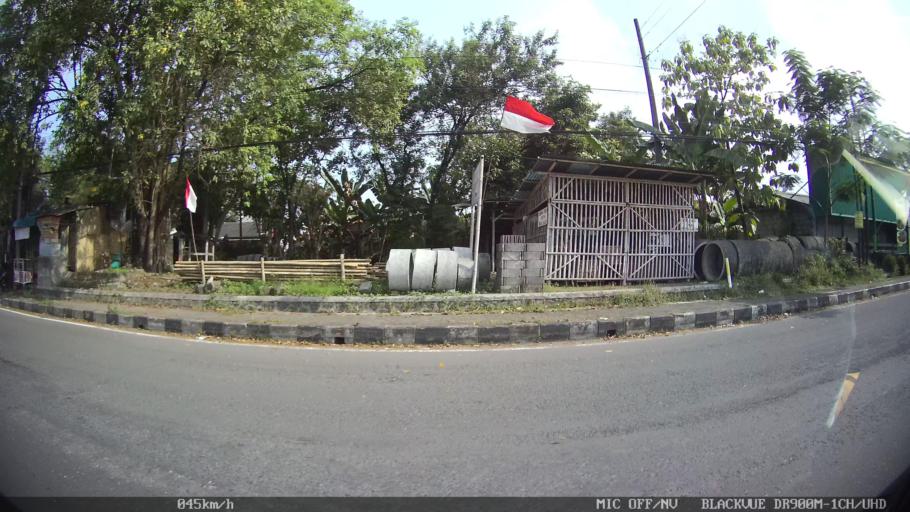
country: ID
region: Daerah Istimewa Yogyakarta
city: Melati
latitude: -7.7509
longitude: 110.3662
